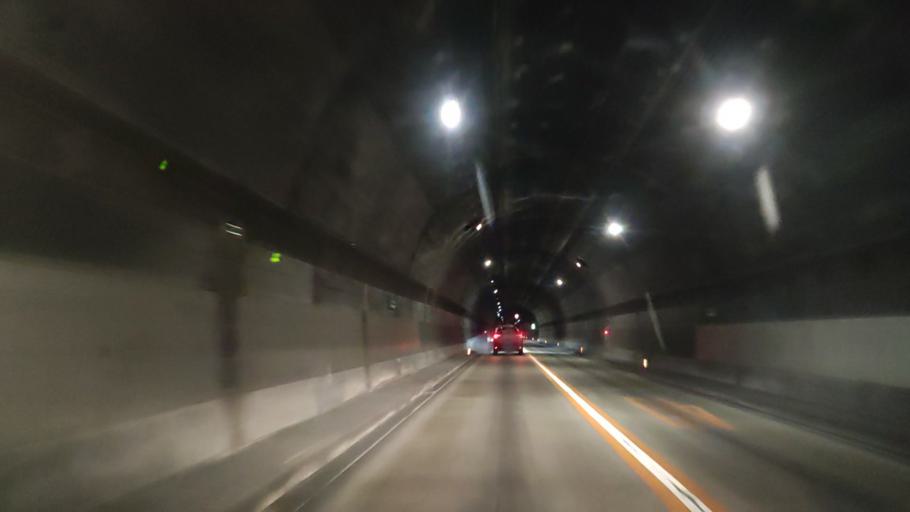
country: JP
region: Tokushima
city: Kamojimacho-jogejima
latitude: 34.1711
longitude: 134.3311
